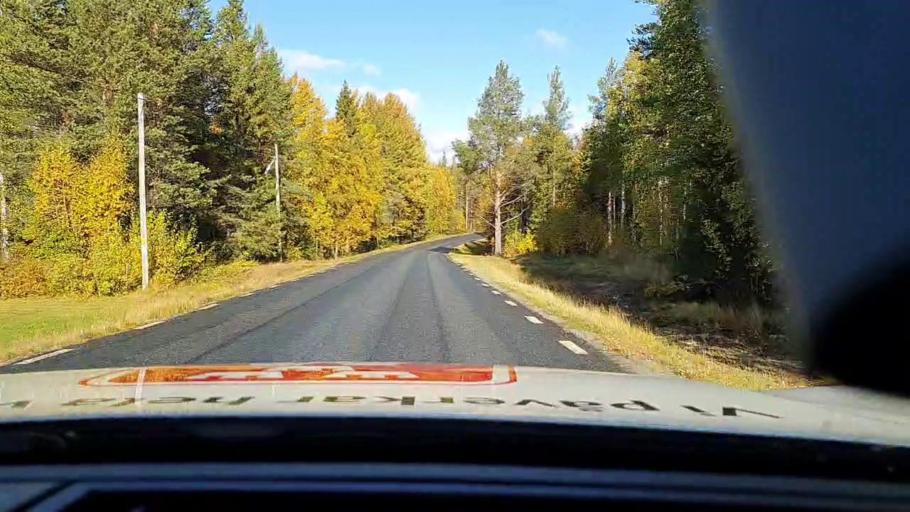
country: SE
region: Vaesterbotten
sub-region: Skelleftea Kommun
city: Langsele
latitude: 64.9997
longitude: 20.0905
